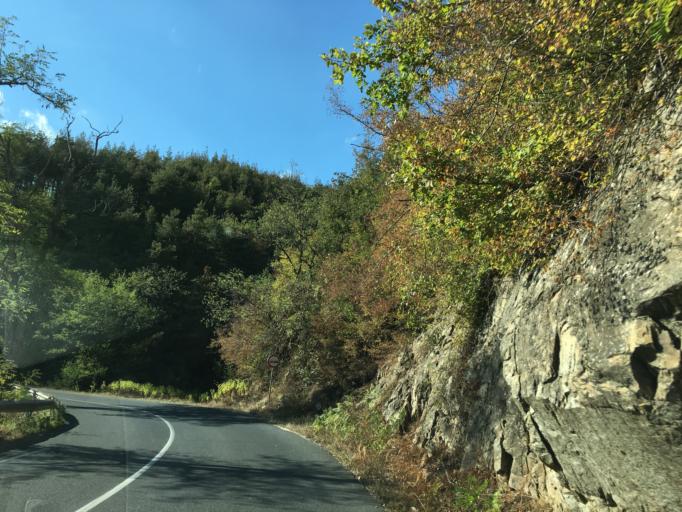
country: BG
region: Smolyan
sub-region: Obshtina Nedelino
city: Nedelino
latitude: 41.4387
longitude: 25.0153
